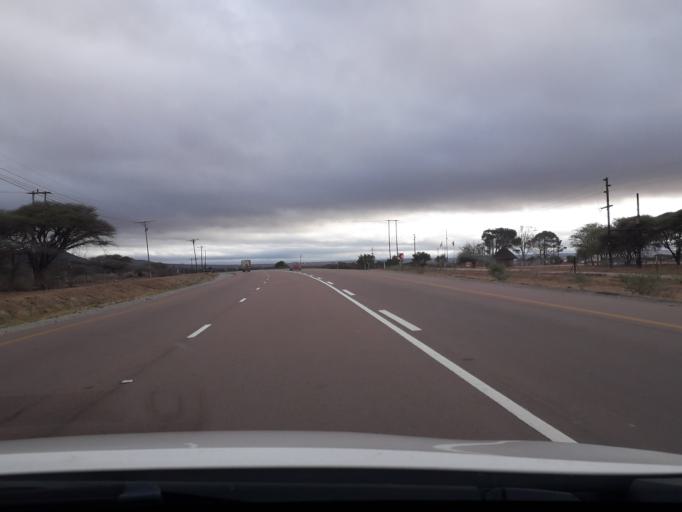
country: ZA
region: Limpopo
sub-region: Capricorn District Municipality
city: Polokwane
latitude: -23.7276
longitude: 29.5869
